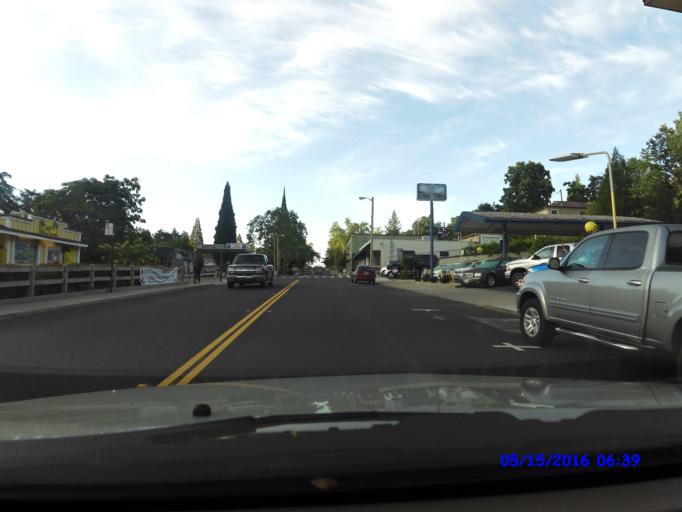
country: US
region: California
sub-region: Tuolumne County
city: Sonora
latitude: 37.9802
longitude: -120.3816
